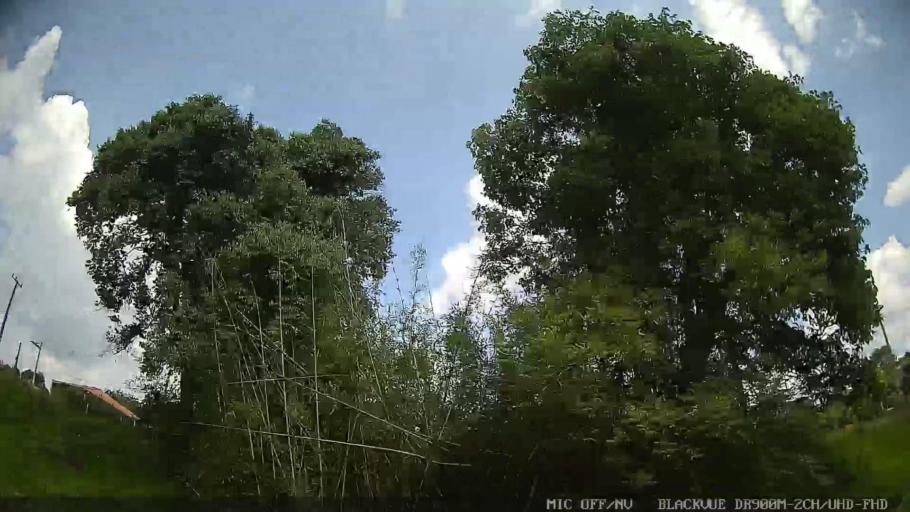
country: BR
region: Sao Paulo
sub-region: Itatiba
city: Itatiba
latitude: -22.9687
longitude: -46.7189
